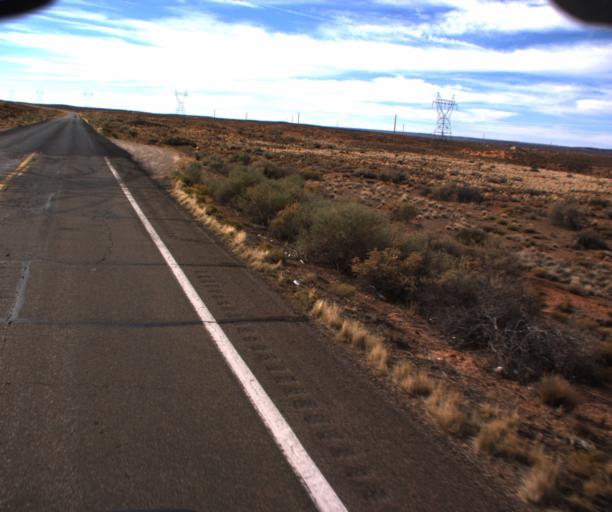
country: US
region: Arizona
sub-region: Coconino County
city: LeChee
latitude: 36.8632
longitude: -111.3392
